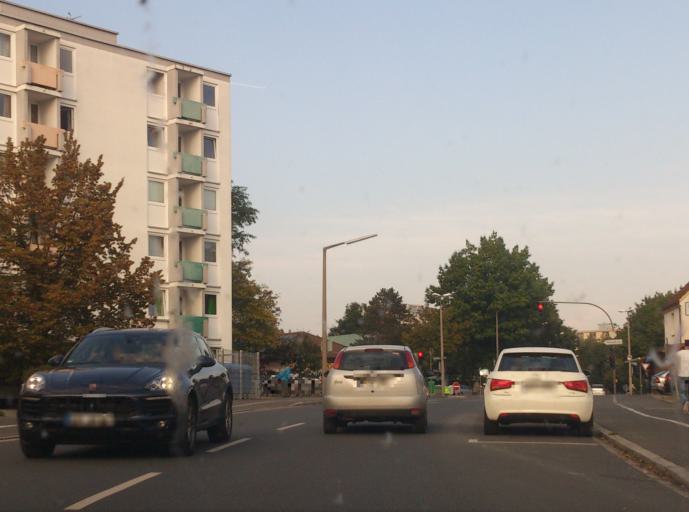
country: DE
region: Bavaria
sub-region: Regierungsbezirk Mittelfranken
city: Buckenhof
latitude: 49.6002
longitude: 11.0384
